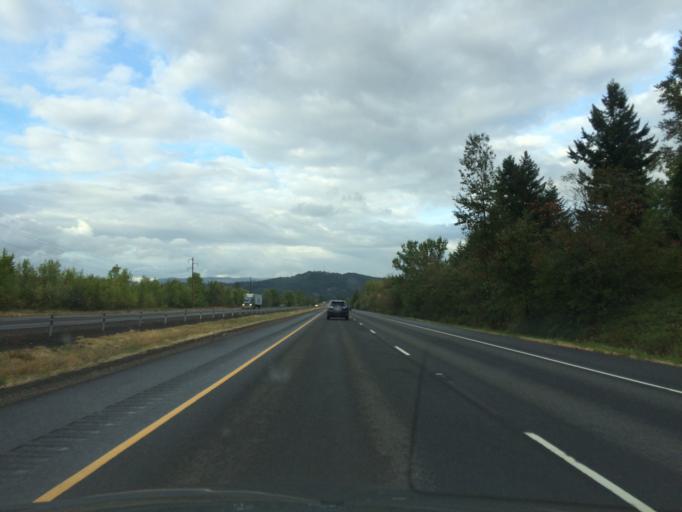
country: US
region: Oregon
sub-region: Lane County
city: Cottage Grove
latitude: 43.7581
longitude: -123.0917
